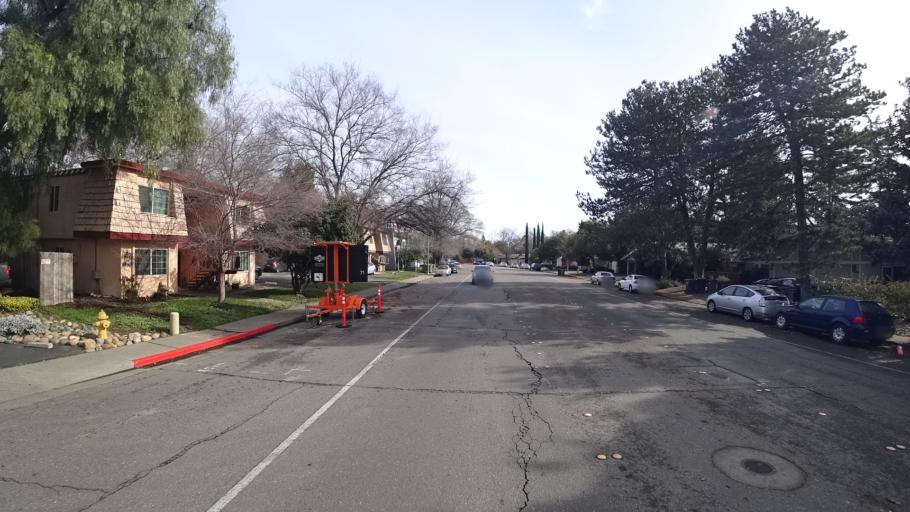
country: US
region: California
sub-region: Yolo County
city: Davis
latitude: 38.5488
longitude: -121.6917
